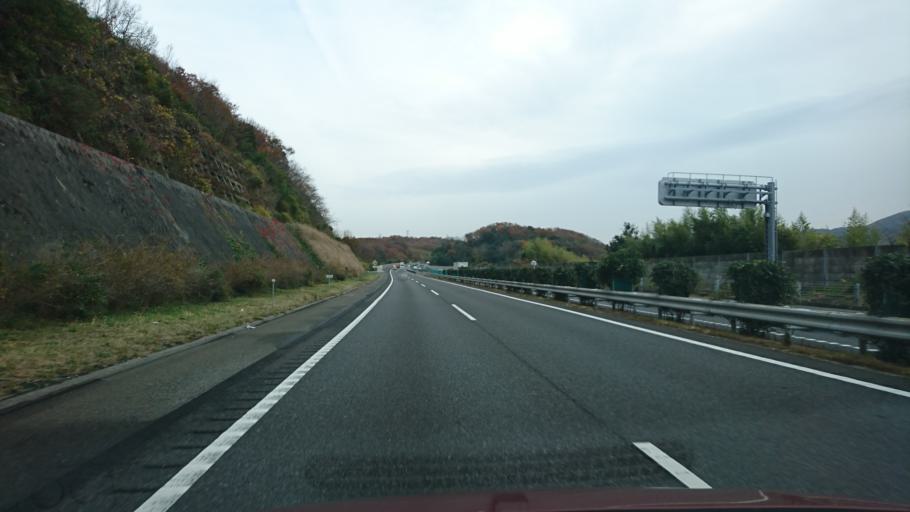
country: JP
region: Hyogo
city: Miki
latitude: 34.8198
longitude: 135.0976
